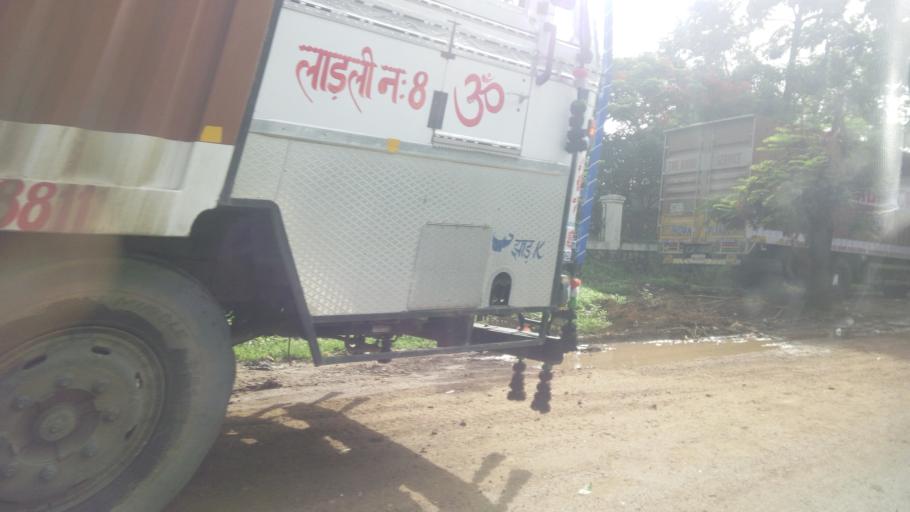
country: IN
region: Tamil Nadu
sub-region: Kancheepuram
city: Nandambakkam
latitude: 13.0002
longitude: 80.0047
